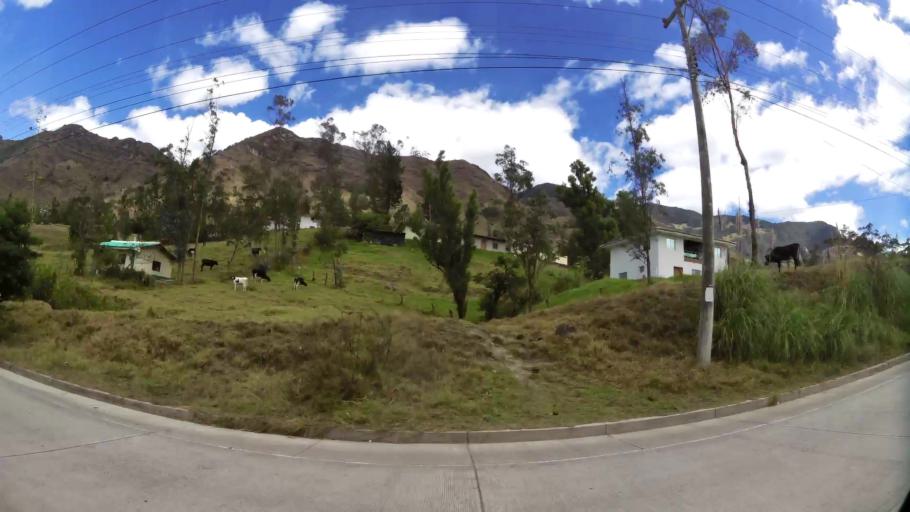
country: EC
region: Azuay
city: Cuenca
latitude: -3.1387
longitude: -79.1370
